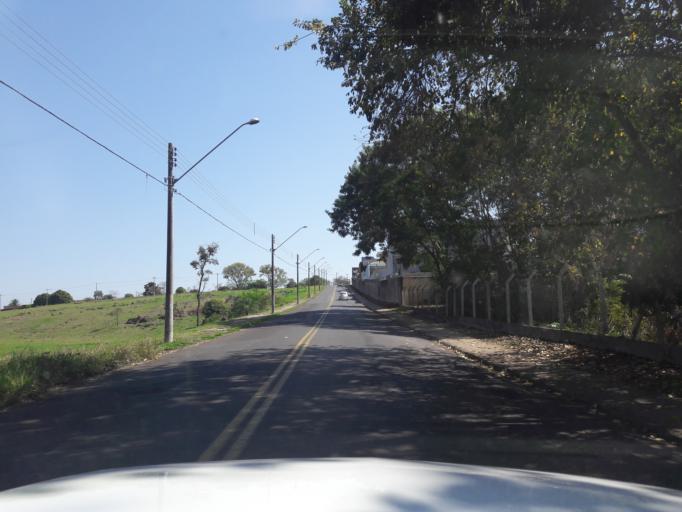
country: BR
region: Sao Paulo
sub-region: Moji-Guacu
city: Mogi-Gaucu
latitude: -22.3612
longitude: -46.9558
